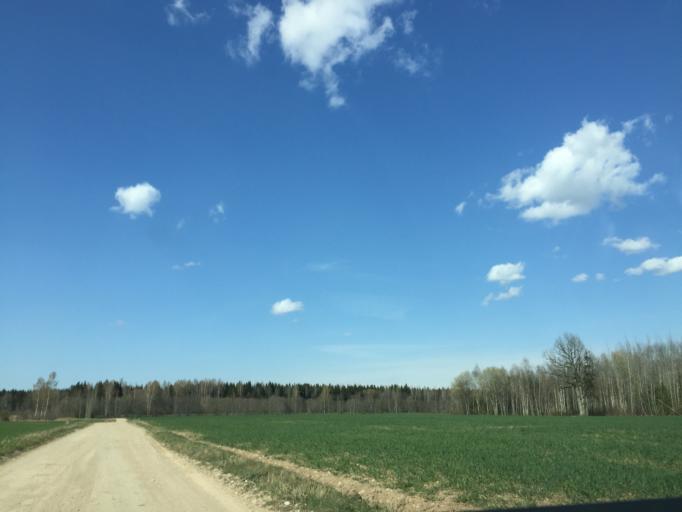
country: LV
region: Lielvarde
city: Lielvarde
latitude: 56.8344
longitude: 24.7984
